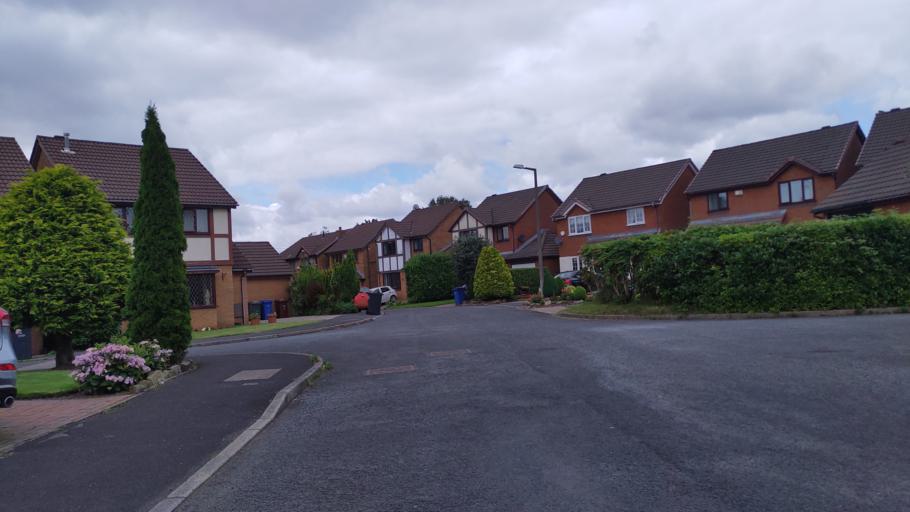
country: GB
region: England
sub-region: Lancashire
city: Chorley
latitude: 53.6392
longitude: -2.6370
